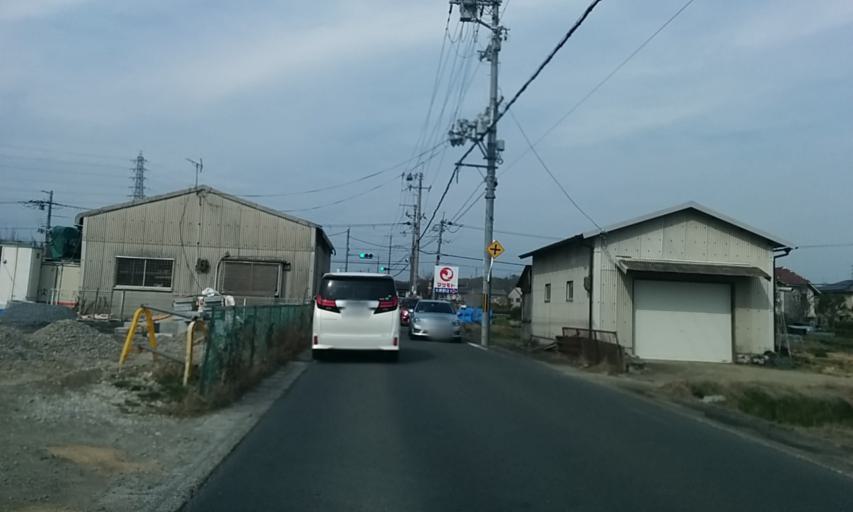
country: JP
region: Kyoto
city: Muko
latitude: 34.9465
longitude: 135.6857
